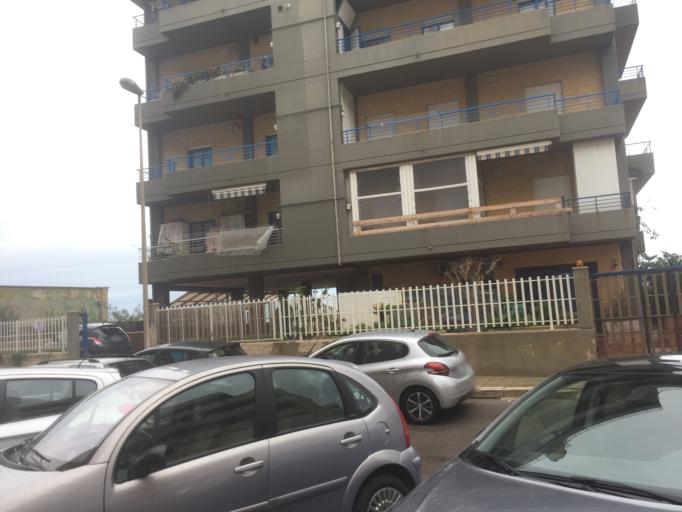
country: IT
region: Apulia
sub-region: Provincia di Bari
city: San Paolo
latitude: 41.1370
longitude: 16.8252
